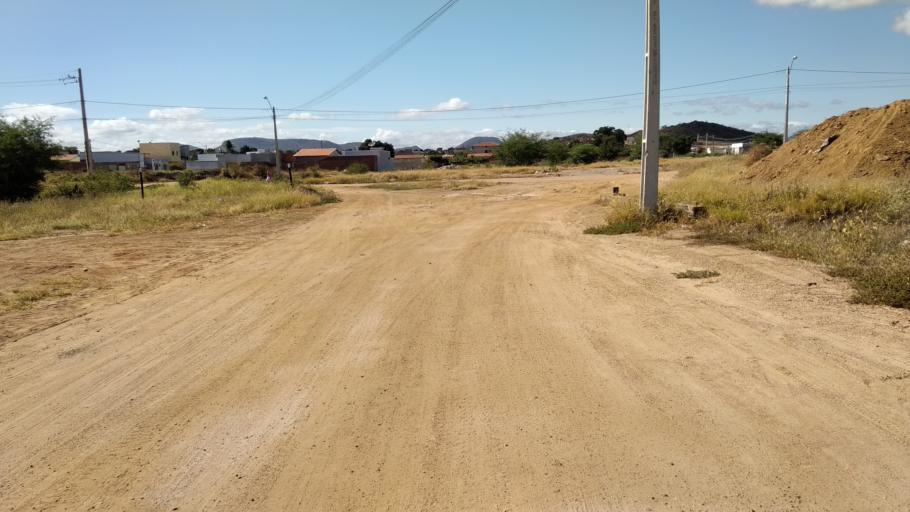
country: BR
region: Bahia
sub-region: Guanambi
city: Guanambi
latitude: -14.2406
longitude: -42.7685
